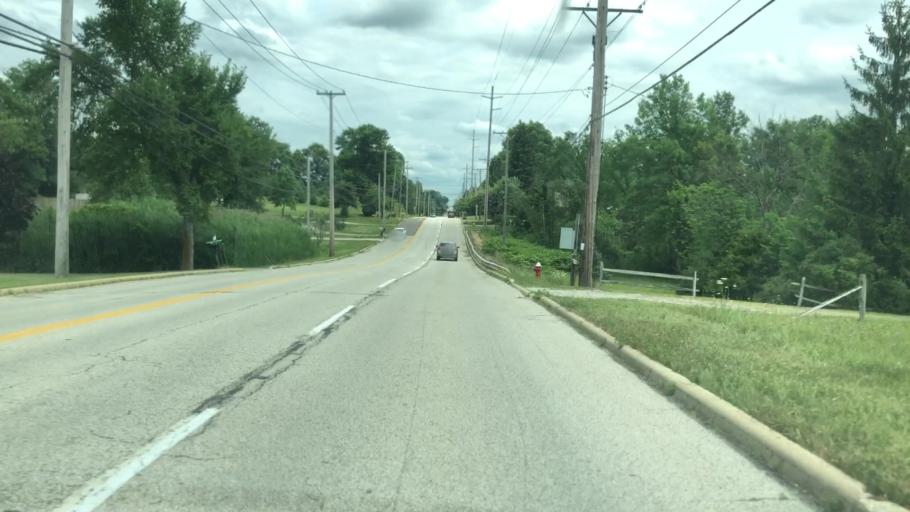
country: US
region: Ohio
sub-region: Summit County
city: Peninsula
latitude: 41.1808
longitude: -81.5338
